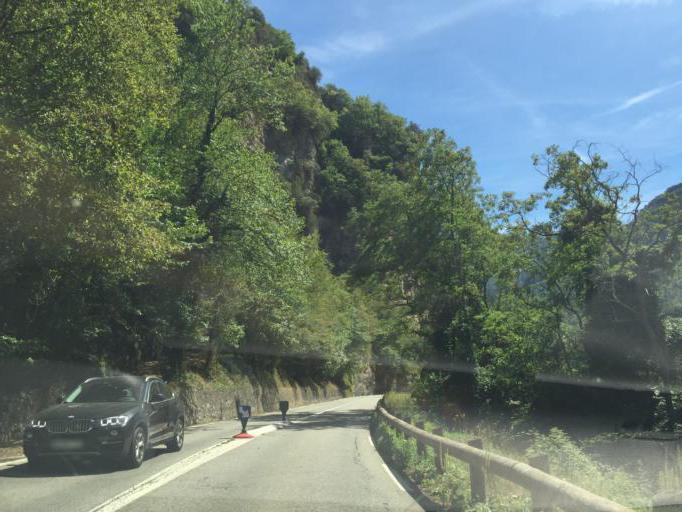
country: FR
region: Provence-Alpes-Cote d'Azur
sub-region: Departement des Alpes-Maritimes
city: Saint-Martin-Vesubie
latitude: 43.9976
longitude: 7.1377
